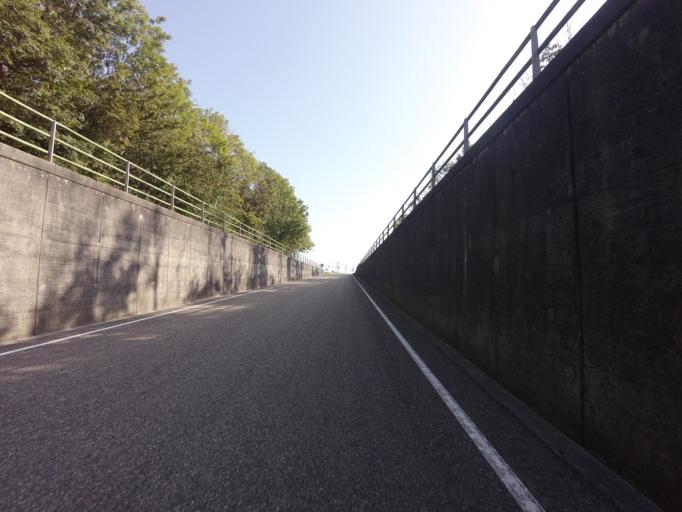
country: NL
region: Friesland
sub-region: Gemeente Franekeradeel
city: Franeker
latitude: 53.2008
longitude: 5.5783
